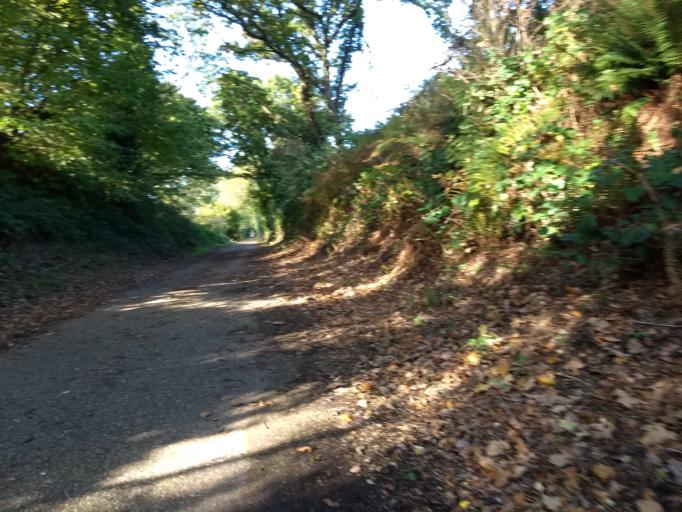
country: GB
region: England
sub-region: Isle of Wight
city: Shanklin
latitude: 50.6294
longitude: -1.2009
